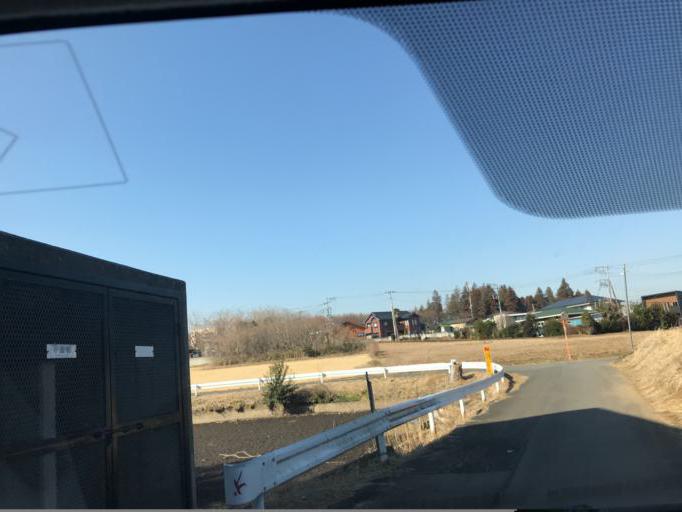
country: JP
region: Ibaraki
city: Naka
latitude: 36.0727
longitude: 140.1308
